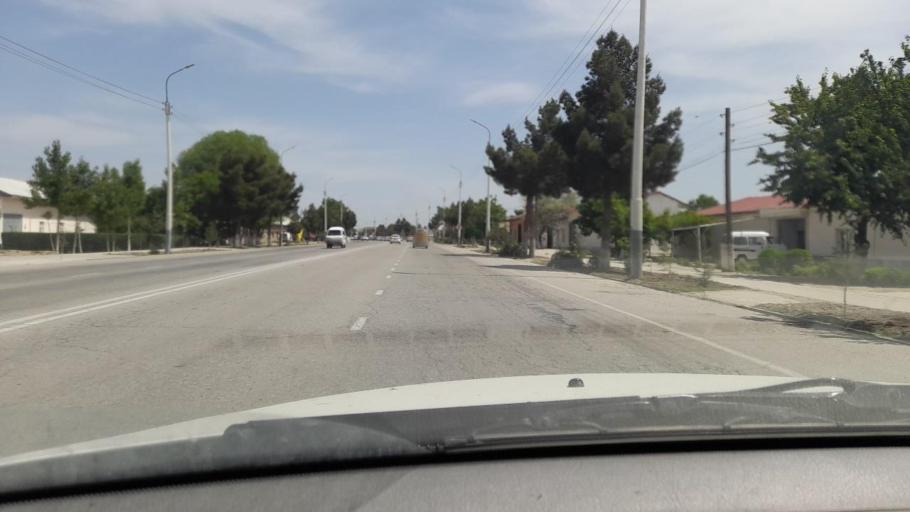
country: UZ
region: Navoiy
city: Karmana Shahri
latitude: 40.1474
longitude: 65.3258
